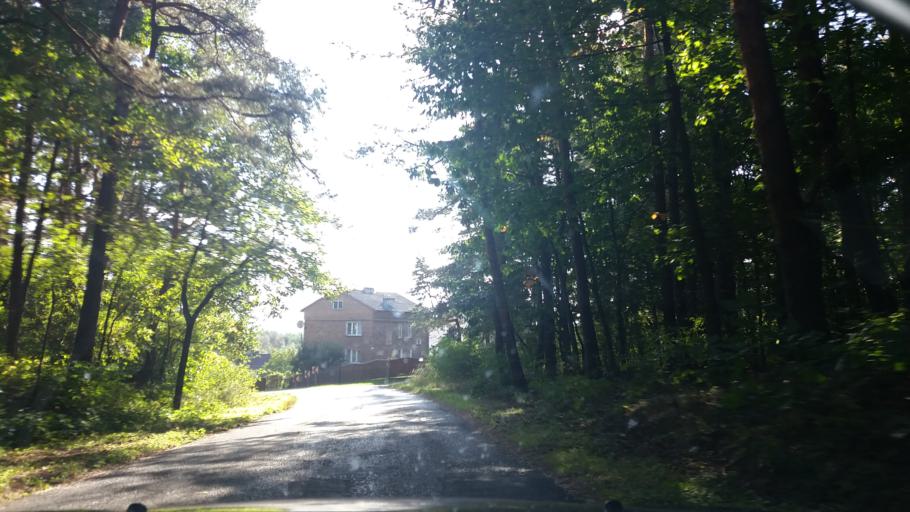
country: PL
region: Lesser Poland Voivodeship
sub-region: Powiat chrzanowski
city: Alwernia
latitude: 50.0277
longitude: 19.5391
